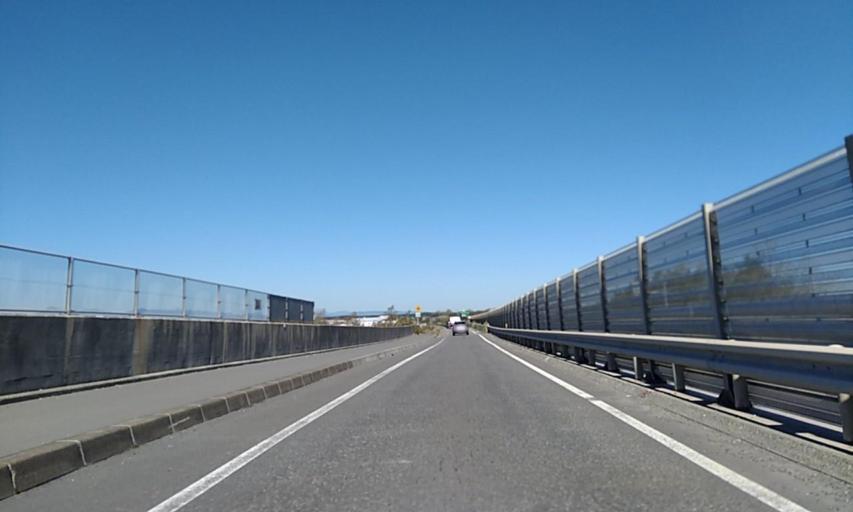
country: JP
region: Hokkaido
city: Tomakomai
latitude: 42.6803
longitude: 141.7079
